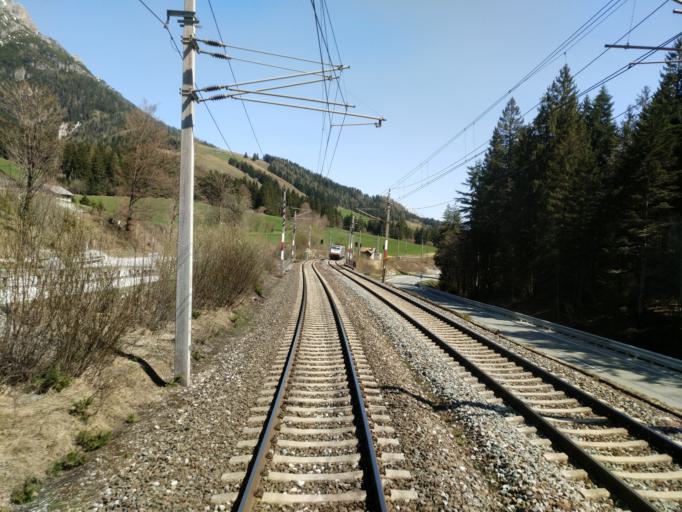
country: AT
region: Tyrol
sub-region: Politischer Bezirk Kitzbuhel
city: Hochfilzen
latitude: 47.4490
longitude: 12.6830
